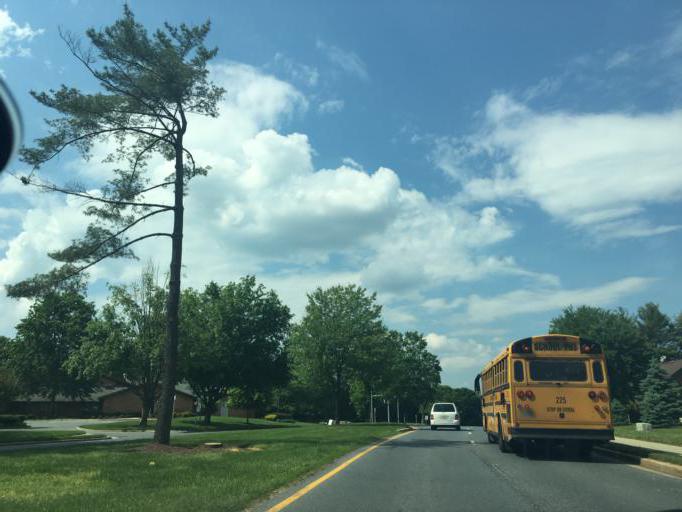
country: US
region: Maryland
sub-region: Montgomery County
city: Montgomery Village
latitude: 39.1856
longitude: -77.1987
